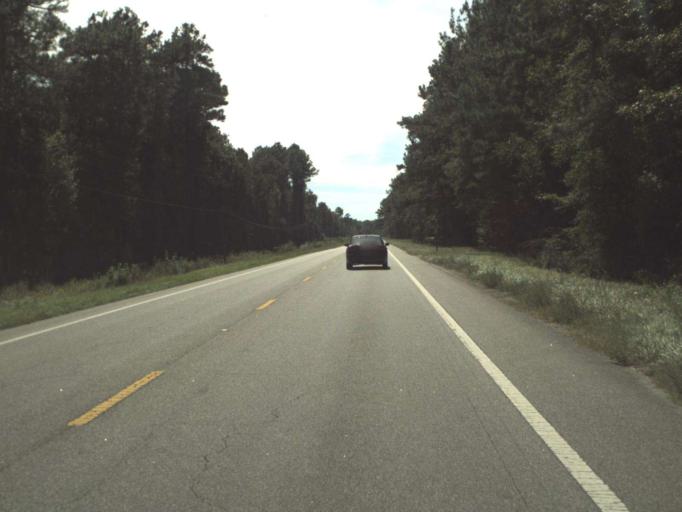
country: US
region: Florida
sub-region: Washington County
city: Chipley
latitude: 30.6511
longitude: -85.5818
